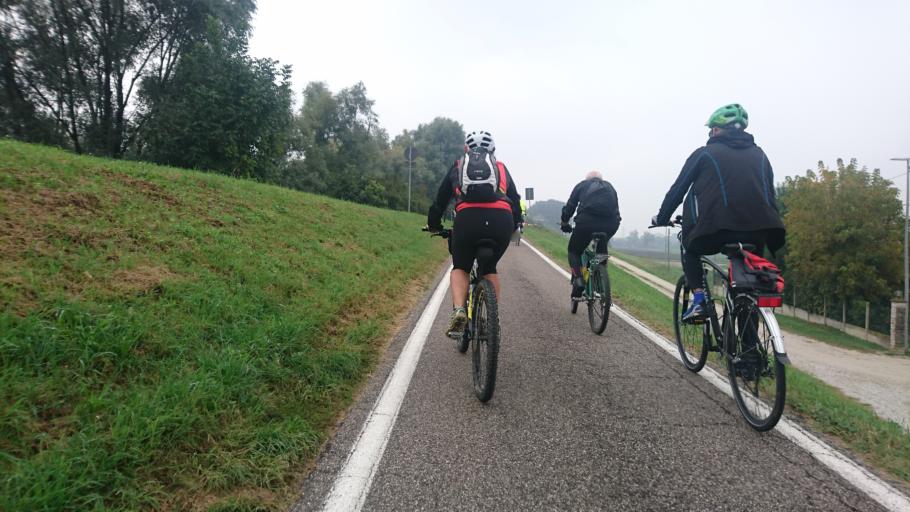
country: IT
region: Veneto
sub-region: Provincia di Padova
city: Stanghella
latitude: 45.1473
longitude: 11.7848
